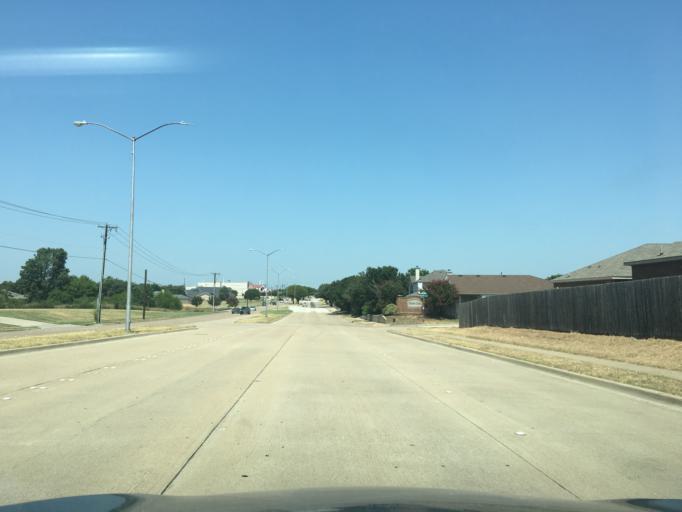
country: US
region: Texas
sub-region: Tarrant County
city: Edgecliff Village
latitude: 32.6238
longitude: -97.3697
